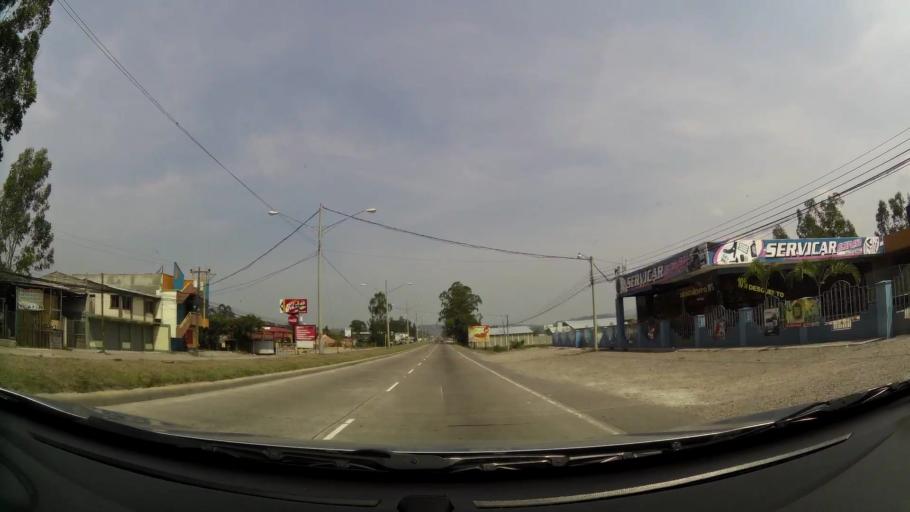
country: HN
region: Comayagua
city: Siguatepeque
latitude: 14.5804
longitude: -87.8413
